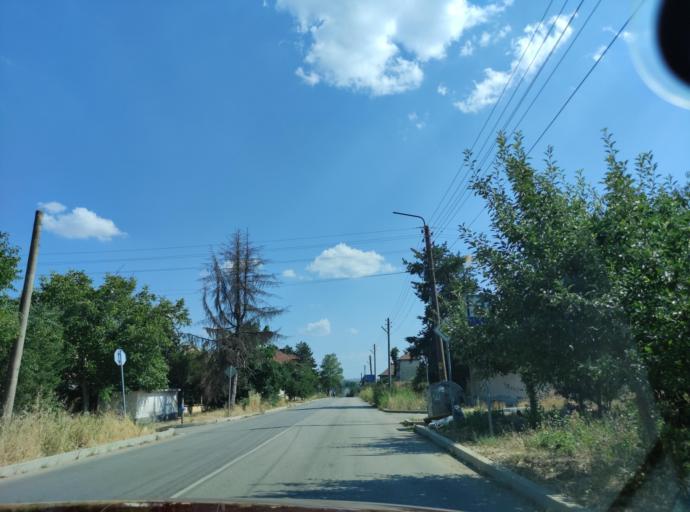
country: BG
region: Pleven
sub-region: Obshtina Cherven Bryag
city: Koynare
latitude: 43.3323
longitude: 24.0667
